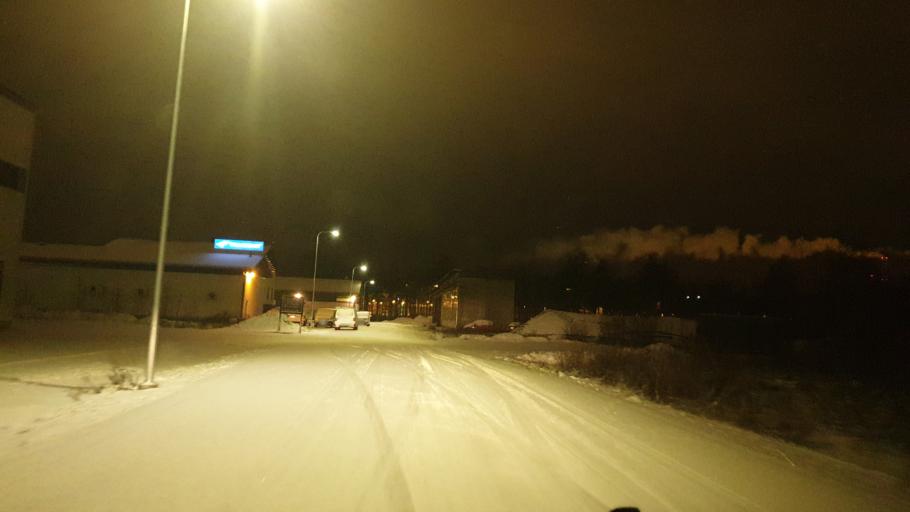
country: FI
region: Northern Ostrobothnia
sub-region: Oulu
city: Oulu
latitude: 64.9953
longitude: 25.4413
